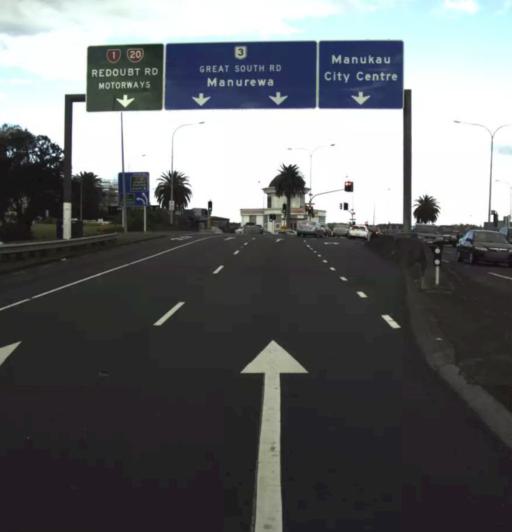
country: NZ
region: Auckland
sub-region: Auckland
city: Manukau City
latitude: -36.9916
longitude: 174.8847
